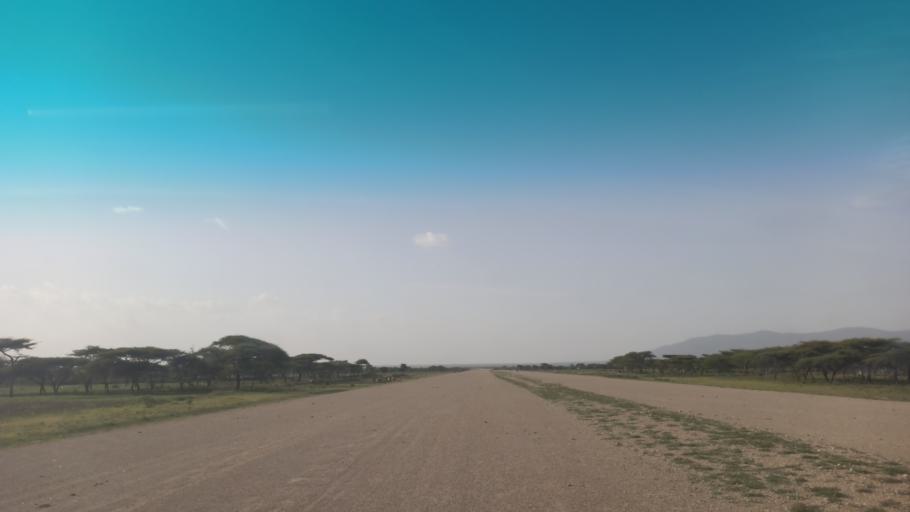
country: ET
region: Oromiya
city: Ziway
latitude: 7.6439
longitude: 38.6820
